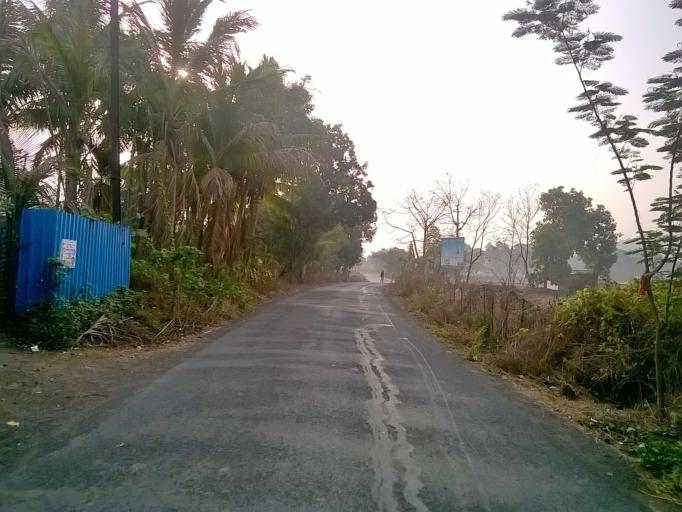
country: IN
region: Maharashtra
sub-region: Raigarh
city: Kalundri
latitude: 19.0145
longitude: 73.1723
